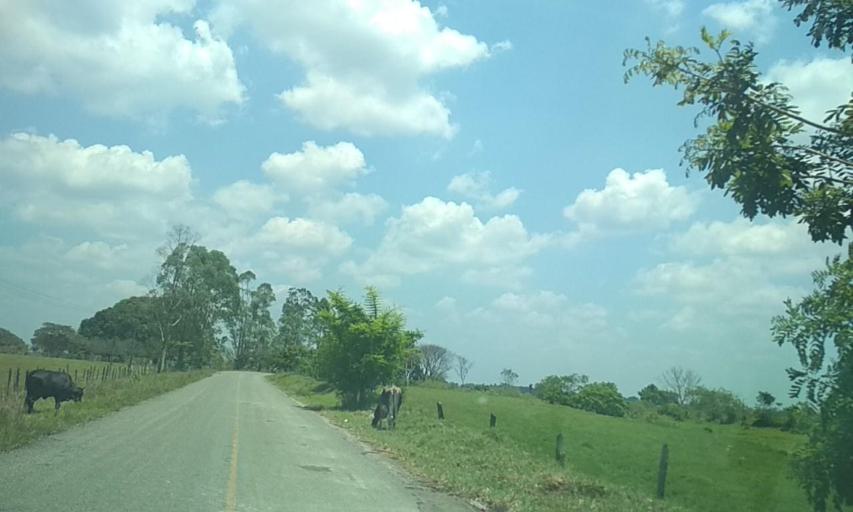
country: MX
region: Tabasco
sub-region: Huimanguillo
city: Francisco Rueda
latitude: 17.8059
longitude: -93.8637
